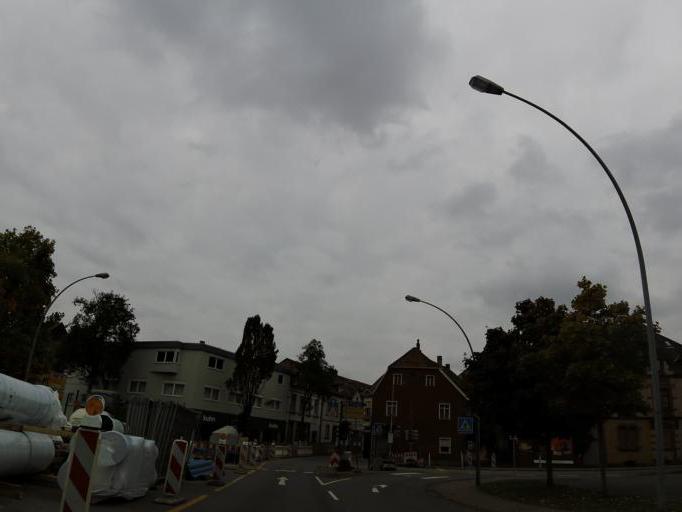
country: DE
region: Saarland
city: Sankt Ingbert
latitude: 49.2822
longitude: 7.1154
